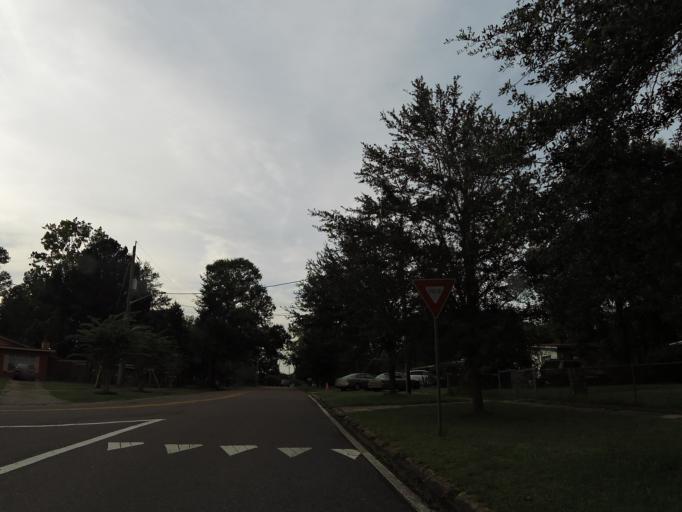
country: US
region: Florida
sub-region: Duval County
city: Jacksonville
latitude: 30.3991
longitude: -81.7195
